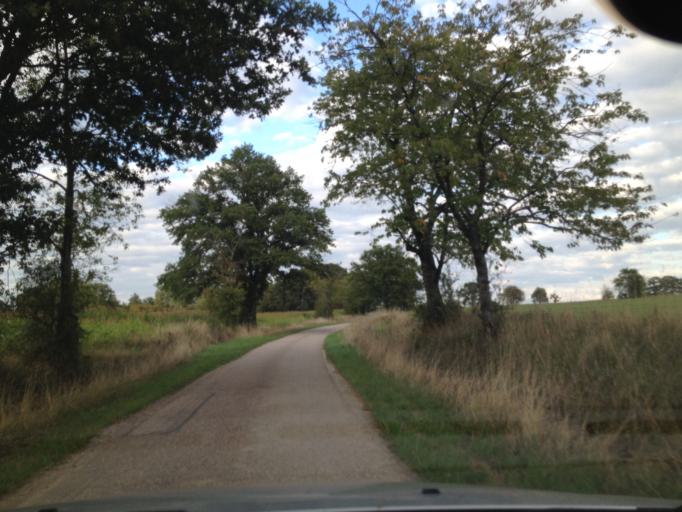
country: FR
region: Lorraine
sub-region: Departement des Vosges
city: Bains-les-Bains
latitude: 47.9845
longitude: 6.1878
